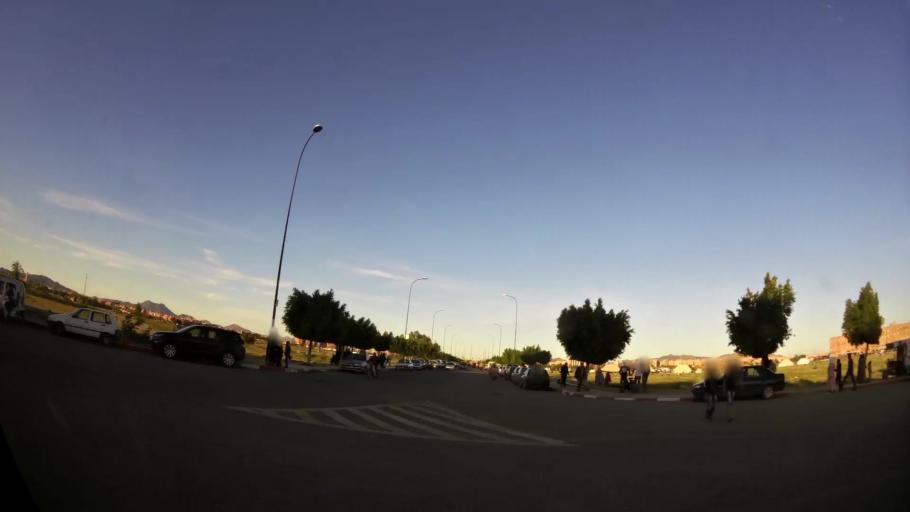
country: MA
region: Marrakech-Tensift-Al Haouz
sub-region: Marrakech
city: Marrakesh
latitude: 31.7520
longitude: -8.1153
